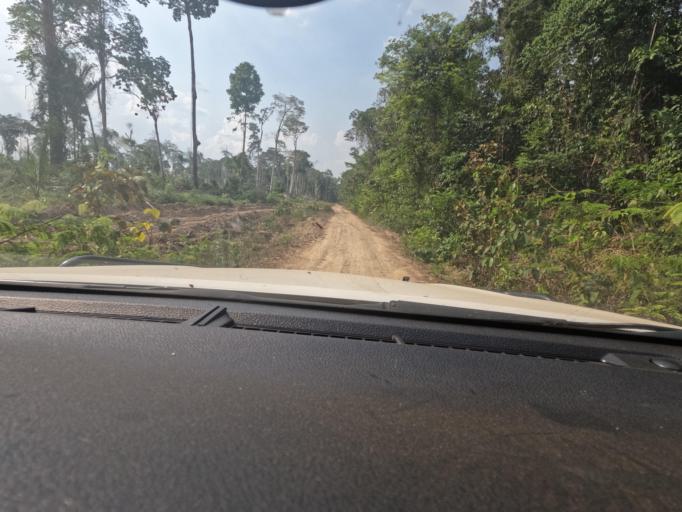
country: BR
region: Rondonia
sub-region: Porto Velho
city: Porto Velho
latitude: -8.6705
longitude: -63.1558
